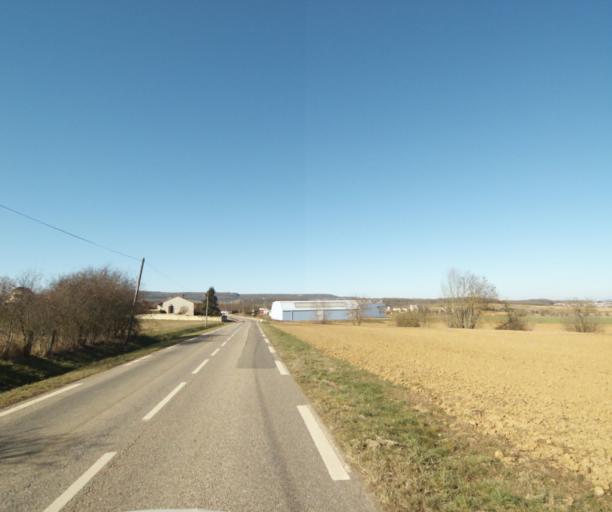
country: FR
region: Lorraine
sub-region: Departement de Meurthe-et-Moselle
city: Fleville-devant-Nancy
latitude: 48.6273
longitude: 6.2146
